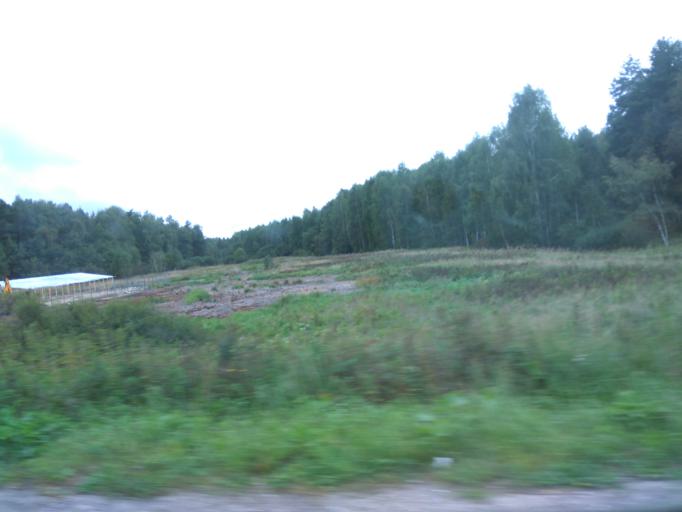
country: RU
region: Moskovskaya
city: Malyshevo
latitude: 55.5194
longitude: 38.3429
